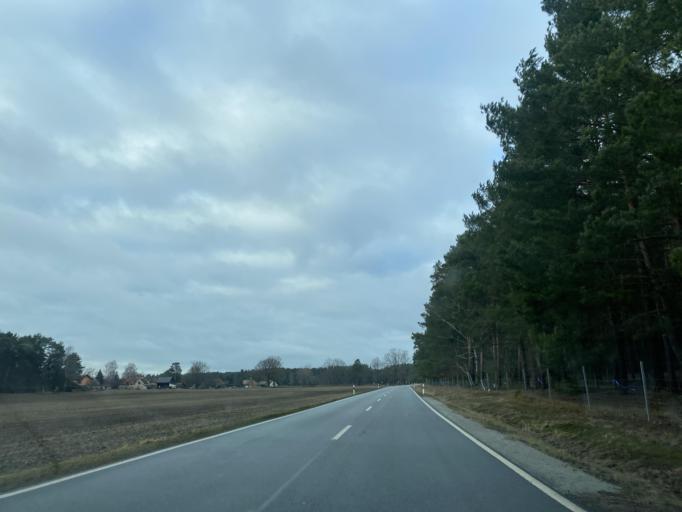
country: PL
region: Lubusz
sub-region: Powiat zarski
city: Leknica
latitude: 51.5098
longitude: 14.7798
